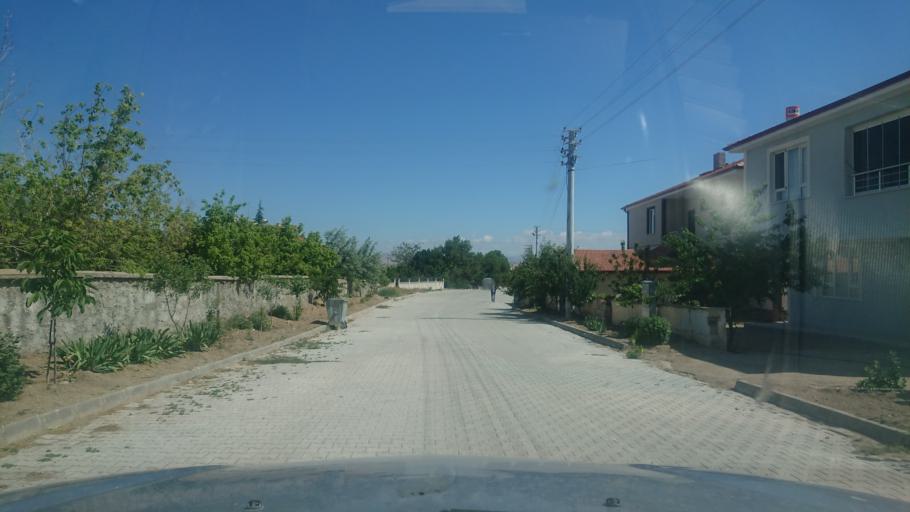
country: TR
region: Aksaray
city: Sariyahsi
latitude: 38.9871
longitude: 33.8457
